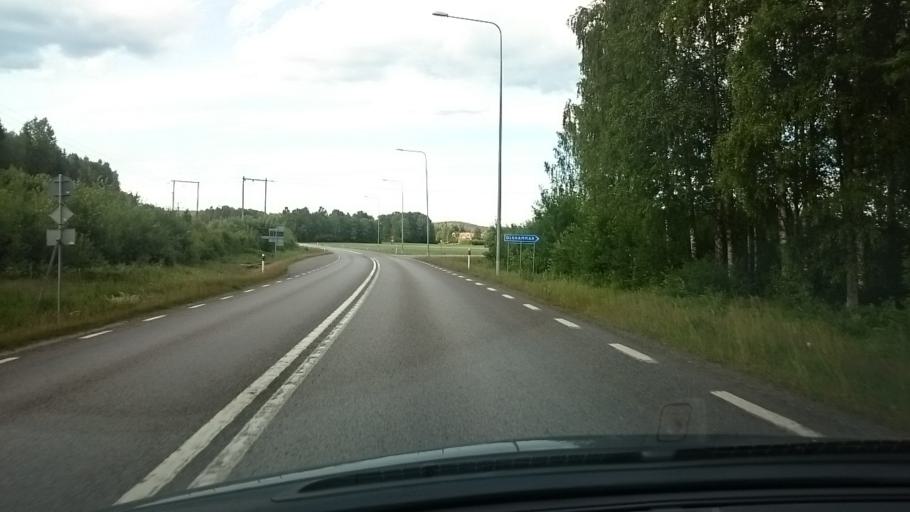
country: SE
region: OErebro
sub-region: Askersunds Kommun
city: Askersund
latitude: 58.7633
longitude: 14.7968
